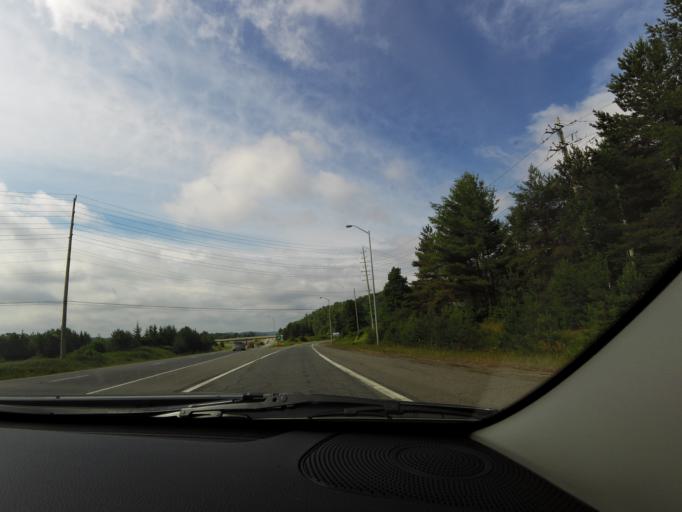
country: CA
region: Ontario
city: Huntsville
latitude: 45.3357
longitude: -79.2359
